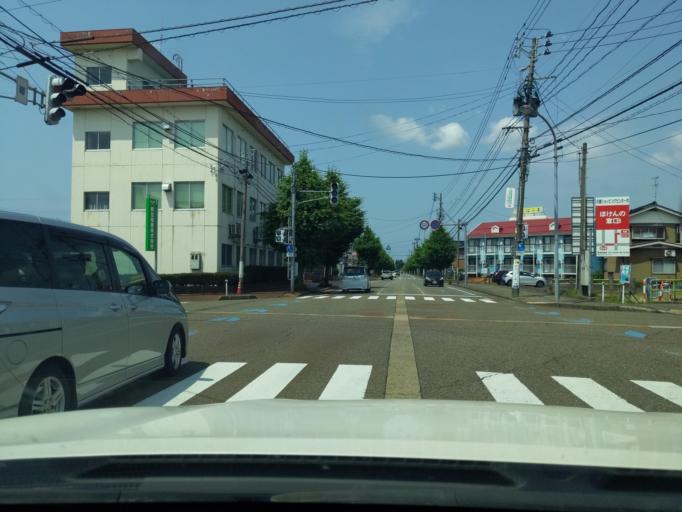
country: JP
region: Niigata
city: Nagaoka
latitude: 37.4311
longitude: 138.8523
